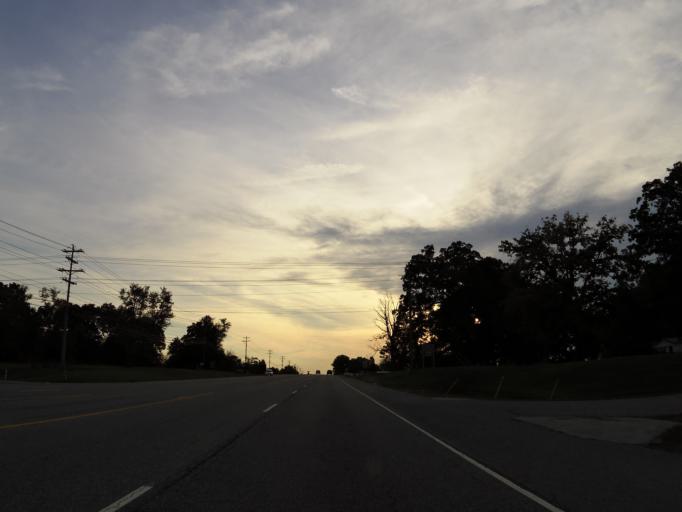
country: US
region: Tennessee
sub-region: Loudon County
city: Greenback
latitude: 35.6472
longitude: -84.1388
